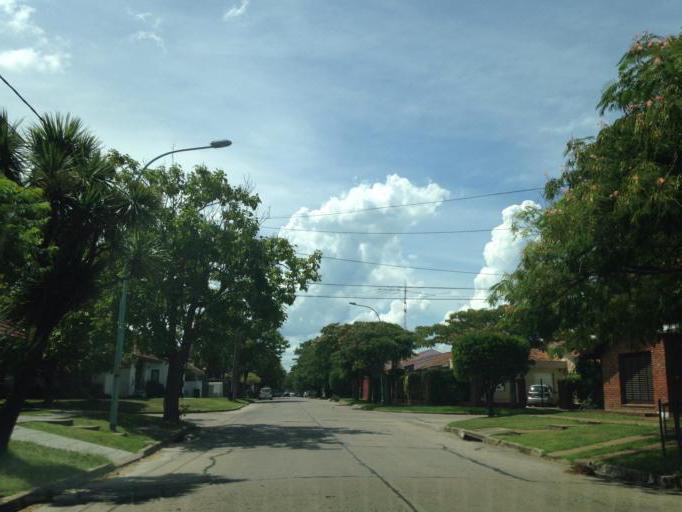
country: AR
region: Buenos Aires
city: Mar del Plata
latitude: -37.9713
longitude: -57.5566
